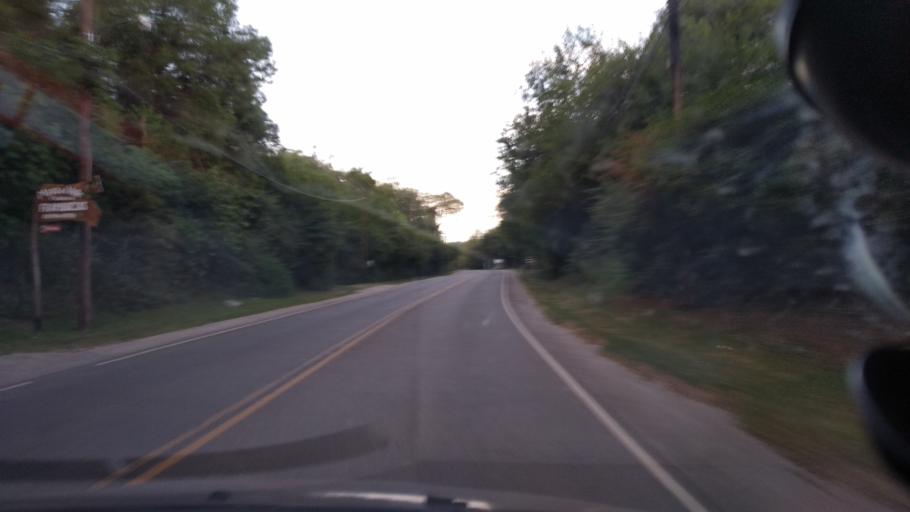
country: AR
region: Cordoba
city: Villa Las Rosas
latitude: -31.9550
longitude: -65.0631
